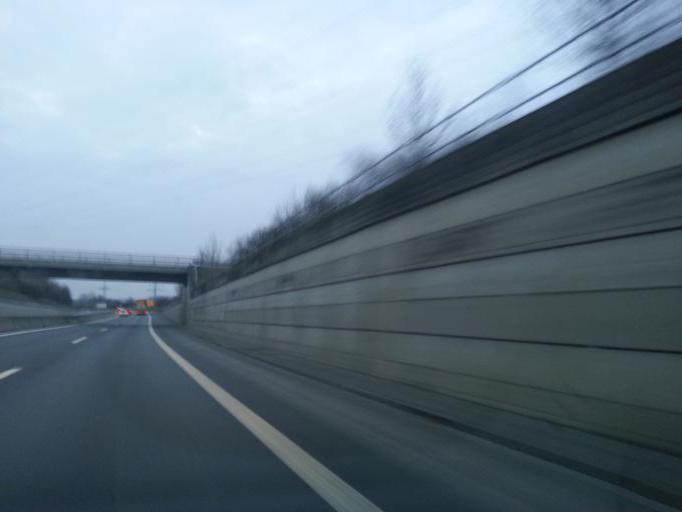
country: DE
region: Baden-Wuerttemberg
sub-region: Tuebingen Region
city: Berg
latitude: 47.8380
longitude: 9.6234
